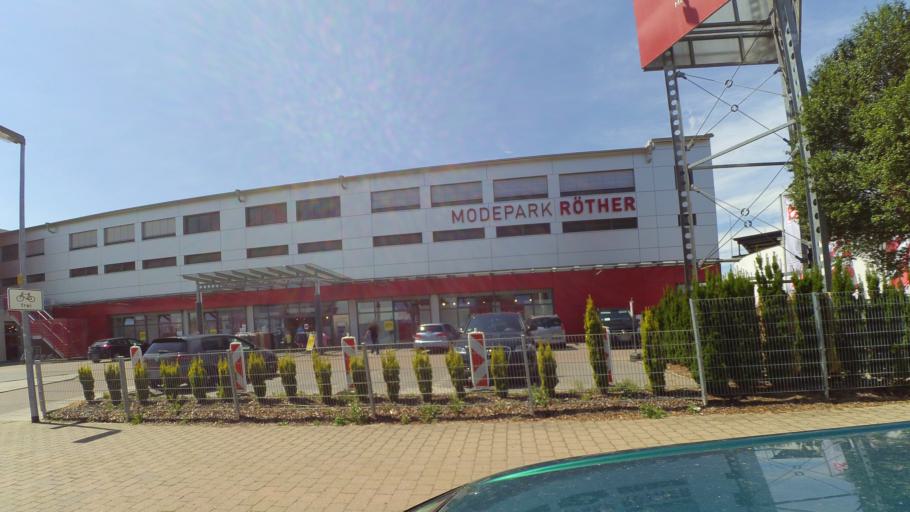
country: DE
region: Baden-Wuerttemberg
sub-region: Regierungsbezirk Stuttgart
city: Michelfeld
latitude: 49.1024
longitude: 9.6930
